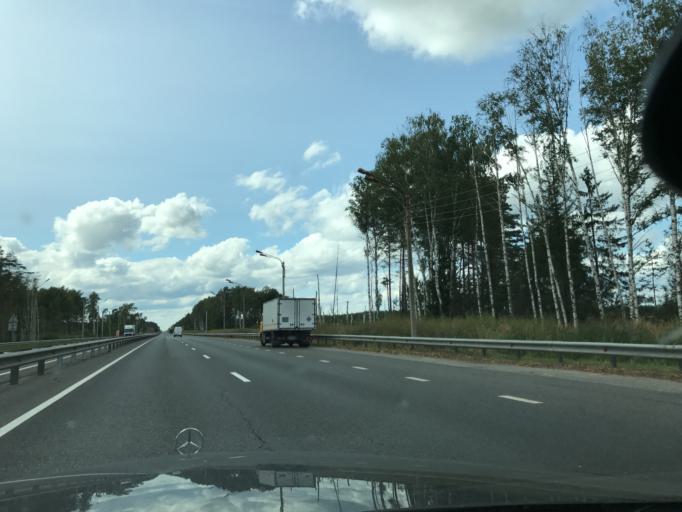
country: RU
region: Vladimir
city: Nikologory
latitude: 56.2364
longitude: 41.9406
